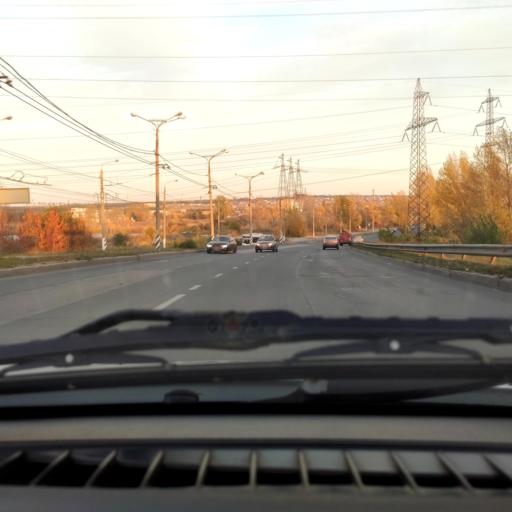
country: RU
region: Samara
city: Zhigulevsk
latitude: 53.4877
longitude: 49.5029
